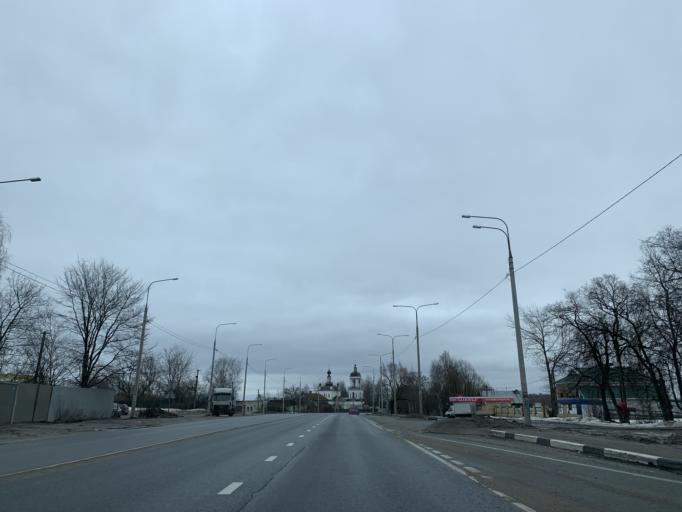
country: RU
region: Jaroslavl
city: Konstantinovskiy
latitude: 57.7656
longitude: 39.6800
